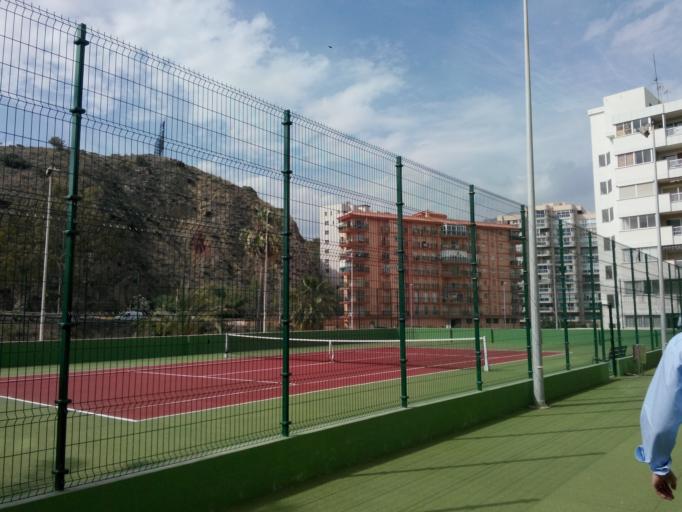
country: ES
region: Andalusia
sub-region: Provincia de Malaga
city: Fuengirola
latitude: 36.5592
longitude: -4.6089
